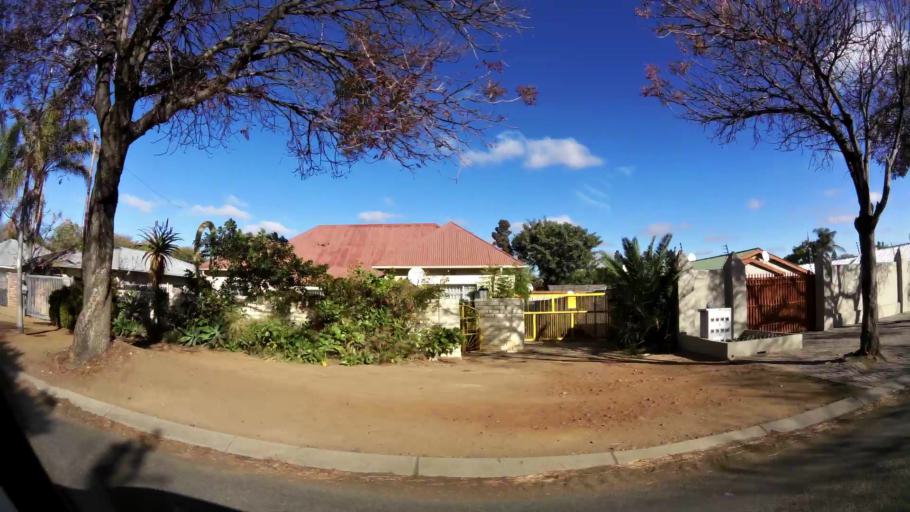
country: ZA
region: Limpopo
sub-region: Capricorn District Municipality
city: Polokwane
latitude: -23.9064
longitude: 29.4592
